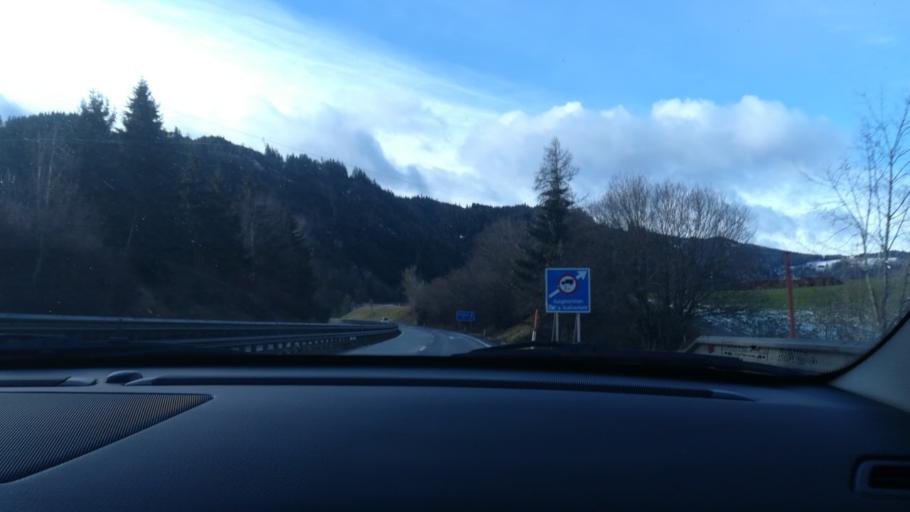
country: AT
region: Styria
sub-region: Politischer Bezirk Murtal
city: Oberweg
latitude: 47.1749
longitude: 14.6339
